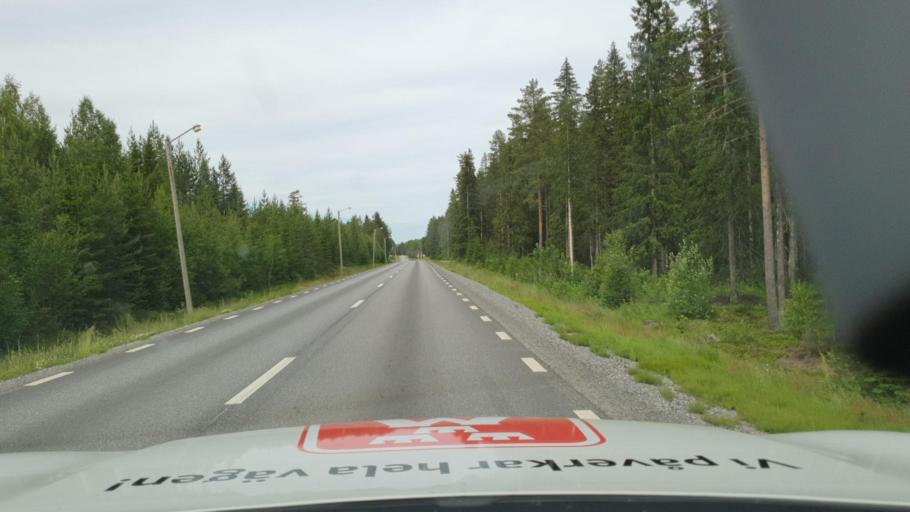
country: SE
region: Vaesterbotten
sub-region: Skelleftea Kommun
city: Burtraesk
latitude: 64.4879
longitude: 20.6234
